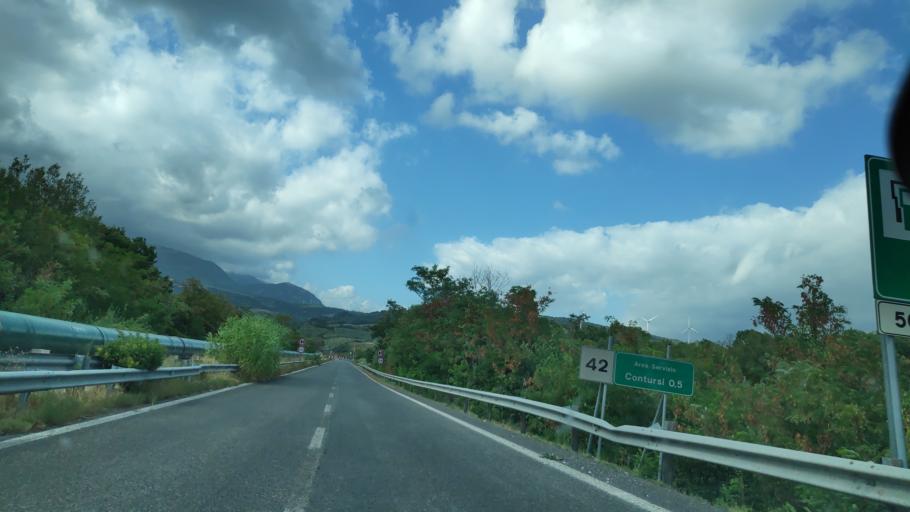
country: IT
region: Campania
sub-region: Provincia di Salerno
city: Serre
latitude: 40.6185
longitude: 15.1812
